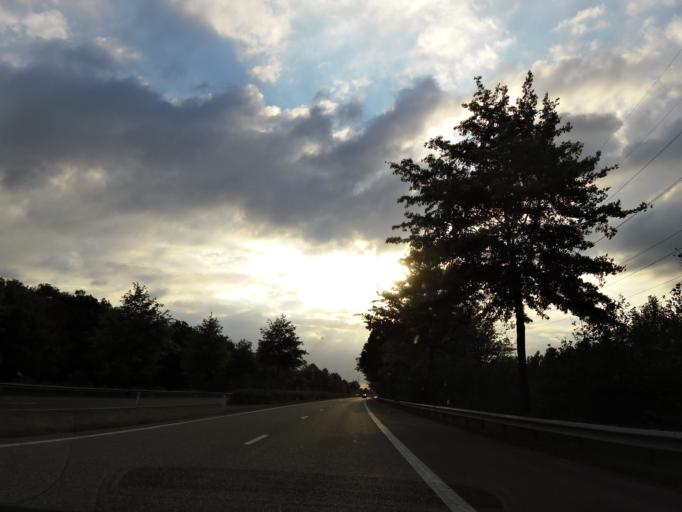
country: BE
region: Flanders
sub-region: Provincie Limburg
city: Diepenbeek
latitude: 50.9342
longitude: 5.4432
